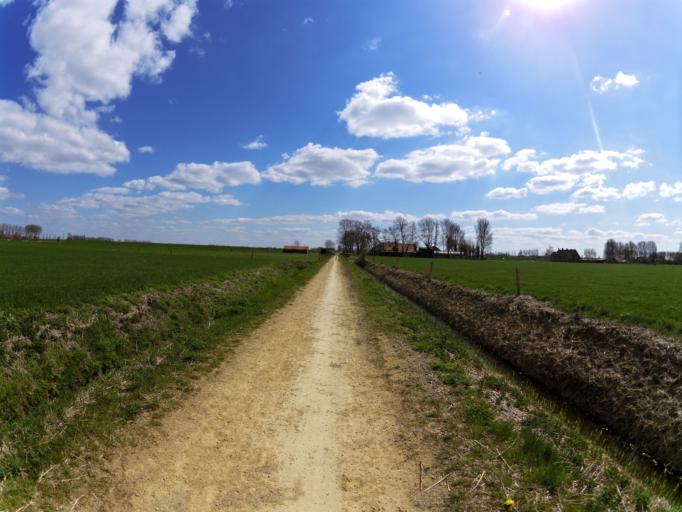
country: NL
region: South Holland
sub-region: Gemeente Hellevoetsluis
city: Nieuw-Helvoet
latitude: 51.8772
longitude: 4.0959
